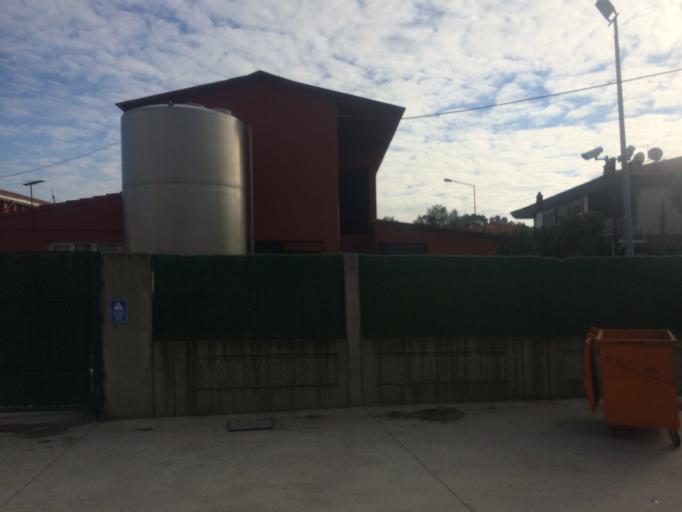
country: TR
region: Izmir
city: Karsiyaka
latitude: 38.4942
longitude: 26.9552
